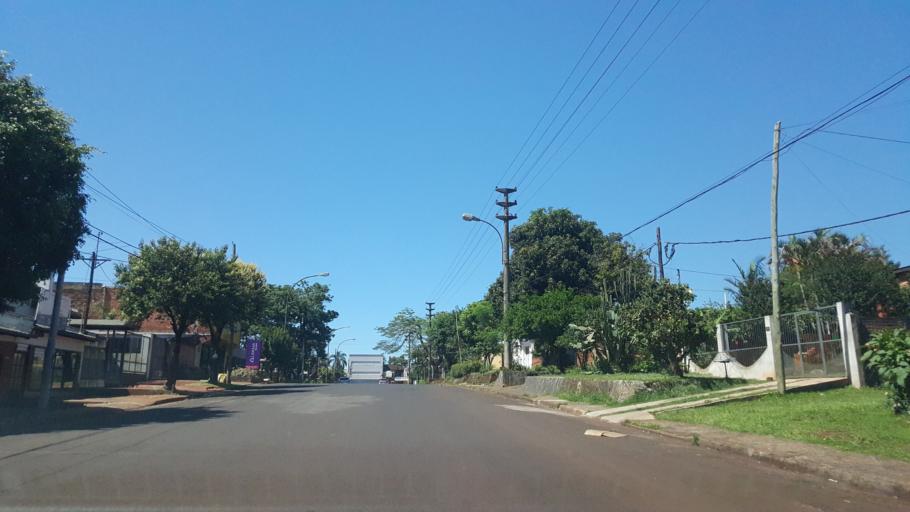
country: AR
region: Misiones
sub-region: Departamento de Capital
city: Posadas
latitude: -27.4025
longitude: -55.9062
